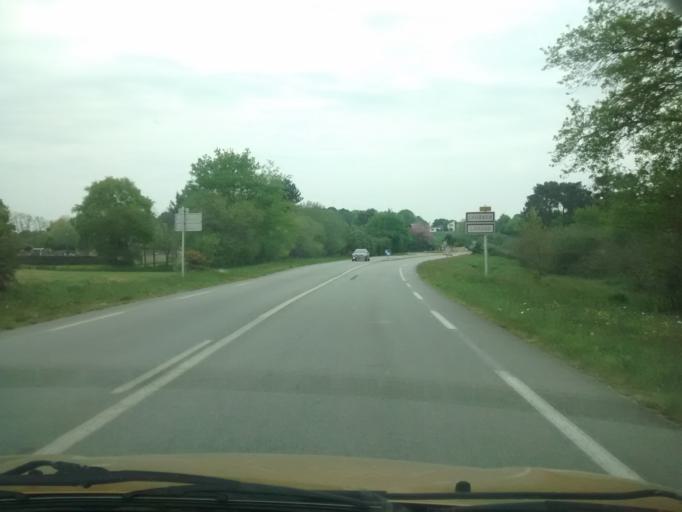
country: FR
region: Brittany
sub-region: Departement du Morbihan
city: Berric
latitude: 47.6134
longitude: -2.5406
